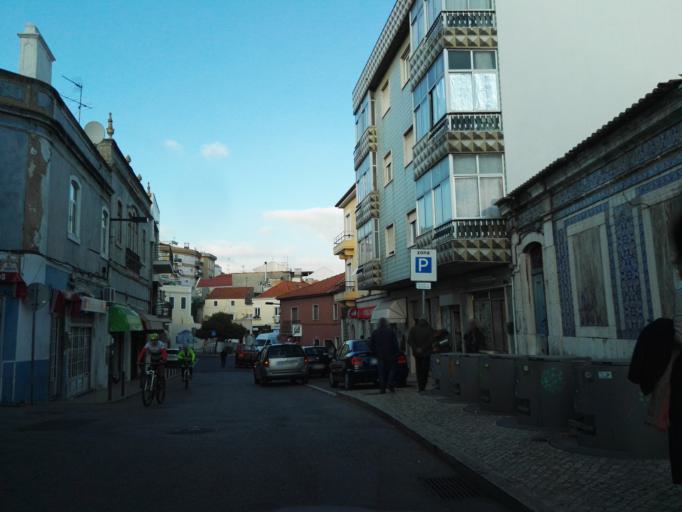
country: PT
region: Lisbon
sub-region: Vila Franca de Xira
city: Povoa de Santa Iria
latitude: 38.8599
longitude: -9.0644
